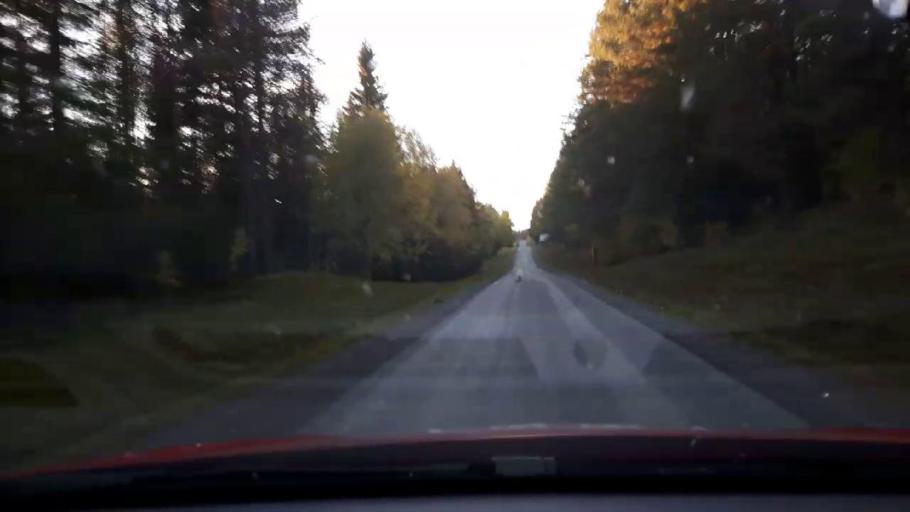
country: SE
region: Jaemtland
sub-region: Krokoms Kommun
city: Krokom
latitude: 63.4807
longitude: 14.3275
